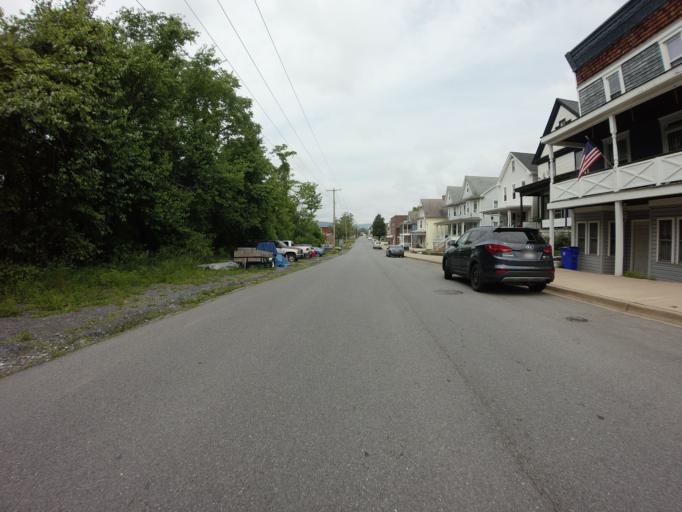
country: US
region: Maryland
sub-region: Frederick County
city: Brunswick
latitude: 39.3112
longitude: -77.6209
